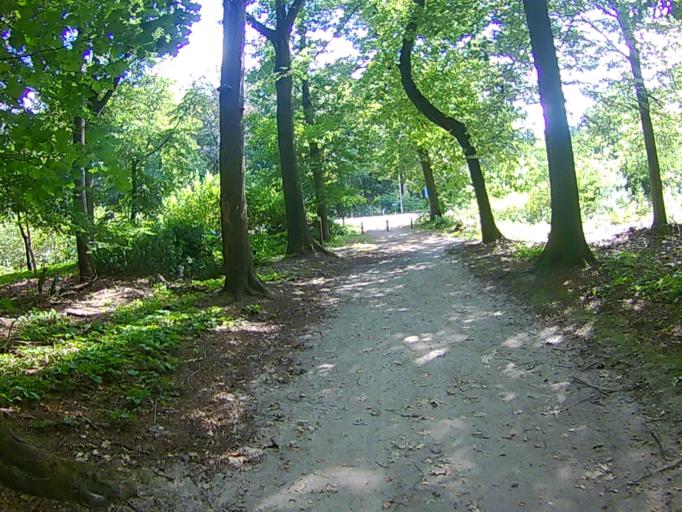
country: BE
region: Flanders
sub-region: Provincie Antwerpen
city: Kapellen
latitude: 51.3368
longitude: 4.4383
